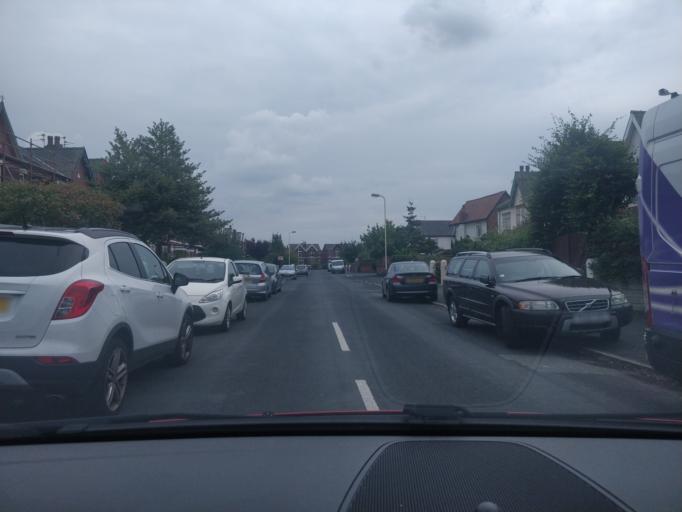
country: GB
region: England
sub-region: Sefton
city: Southport
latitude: 53.6525
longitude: -2.9692
